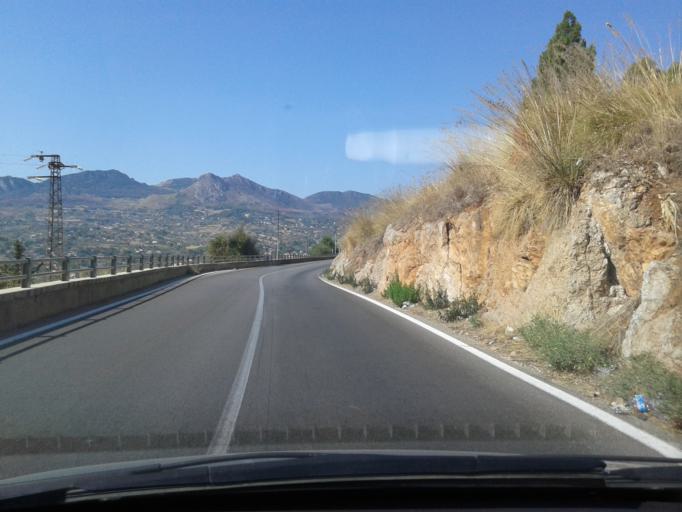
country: IT
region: Sicily
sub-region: Palermo
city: Cannizzaro-Favara
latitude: 38.0602
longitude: 13.2615
